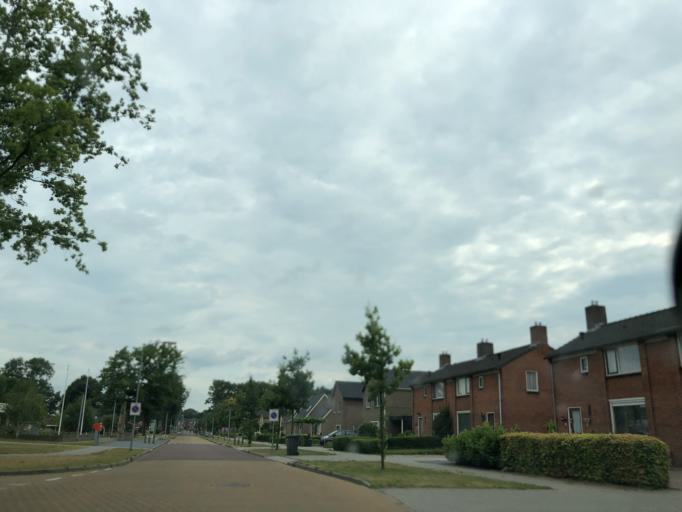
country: NL
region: Drenthe
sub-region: Gemeente Borger-Odoorn
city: Borger
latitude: 52.9232
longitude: 6.7958
